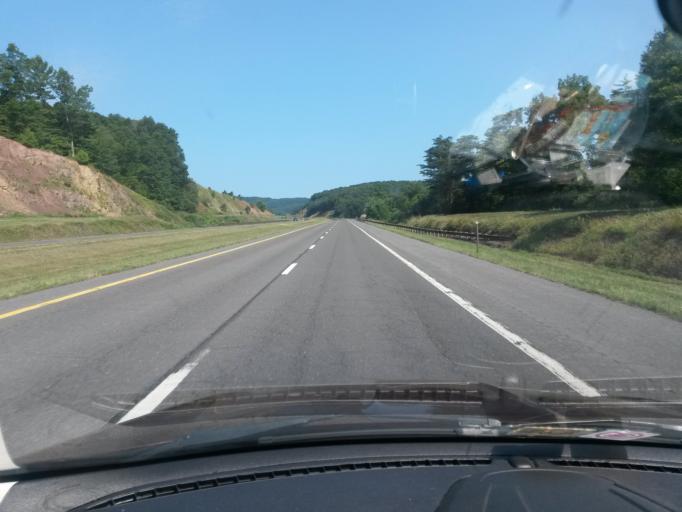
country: US
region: West Virginia
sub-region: Hardy County
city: Moorefield
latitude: 39.0574
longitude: -78.7833
